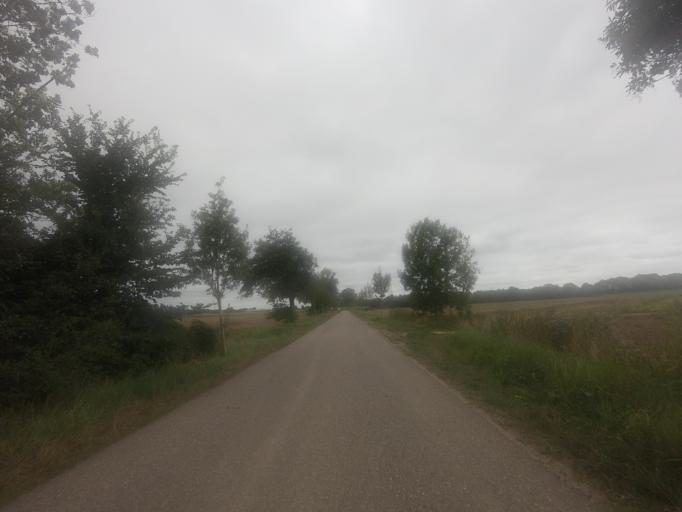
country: NL
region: North Brabant
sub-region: Gemeente Grave
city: Grave
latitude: 51.7870
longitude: 5.7517
